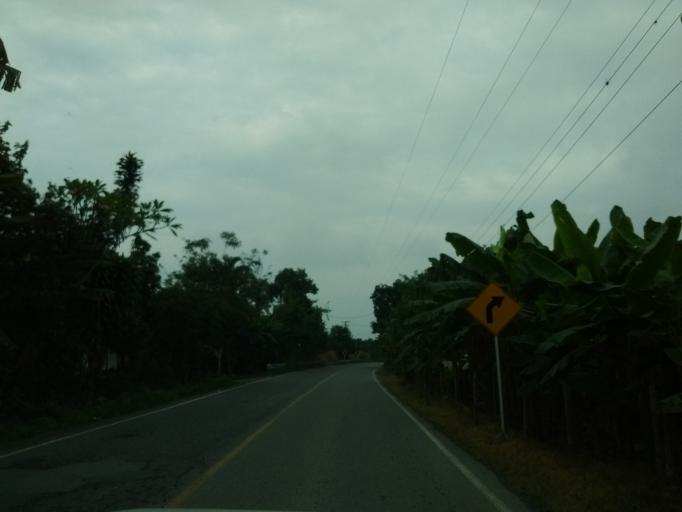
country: CO
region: Cauca
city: Padilla
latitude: 3.2287
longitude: -76.3313
